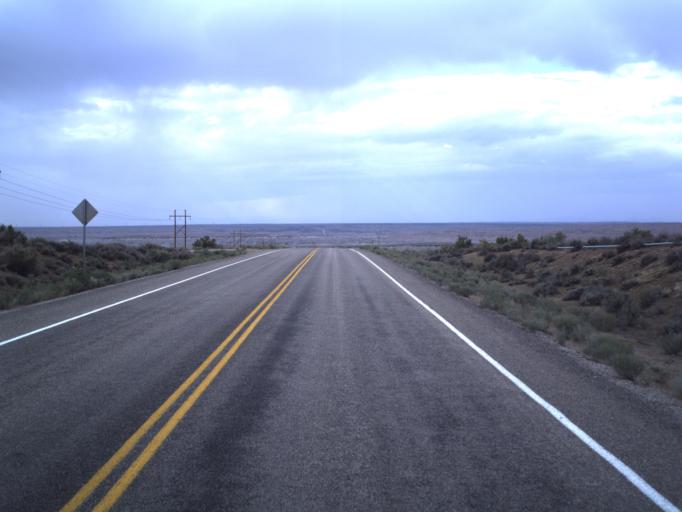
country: US
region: Colorado
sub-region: Rio Blanco County
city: Rangely
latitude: 40.0785
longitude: -109.2107
